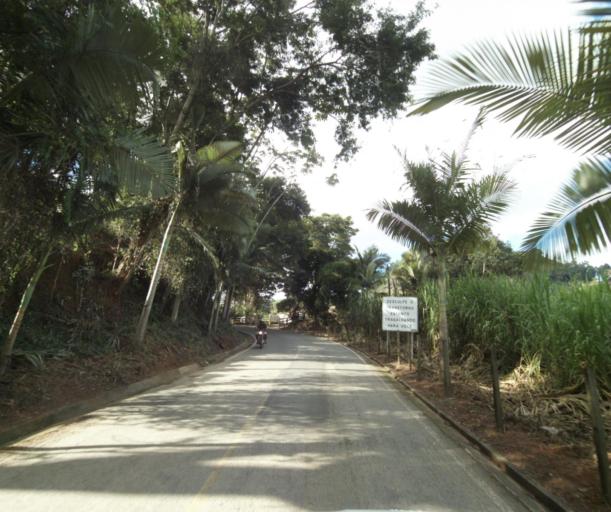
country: BR
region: Espirito Santo
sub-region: Irupi
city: Irupi
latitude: -20.5387
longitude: -41.6684
